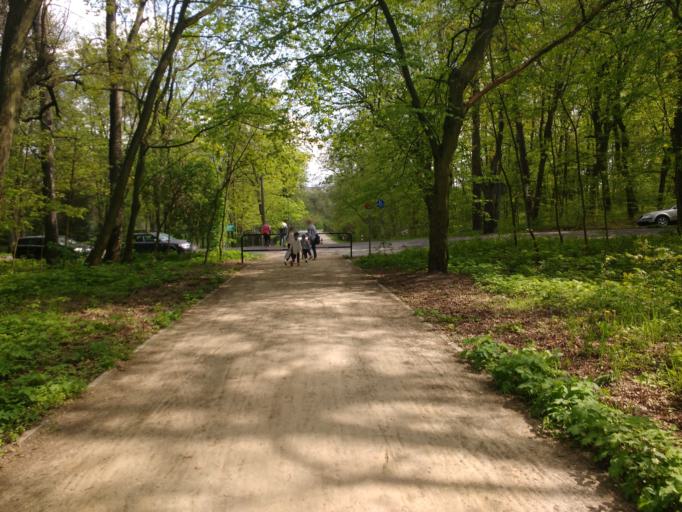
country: PL
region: Kujawsko-Pomorskie
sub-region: Grudziadz
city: Grudziadz
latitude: 53.5077
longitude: 18.7634
